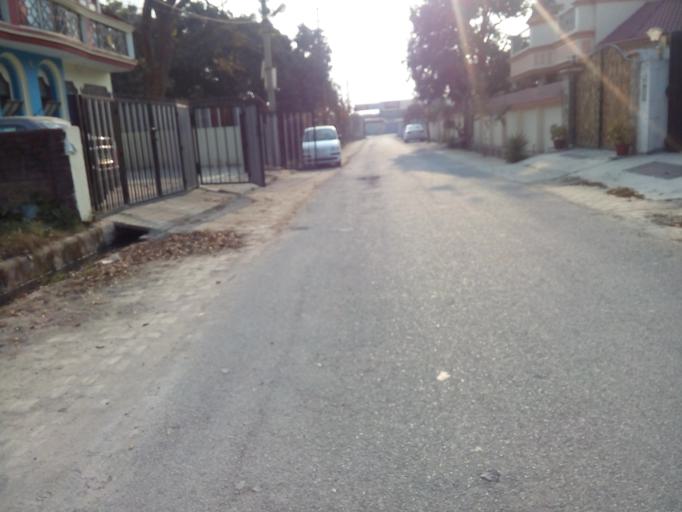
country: IN
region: Uttarakhand
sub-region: Dehradun
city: Dehradun
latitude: 30.3064
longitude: 78.0117
